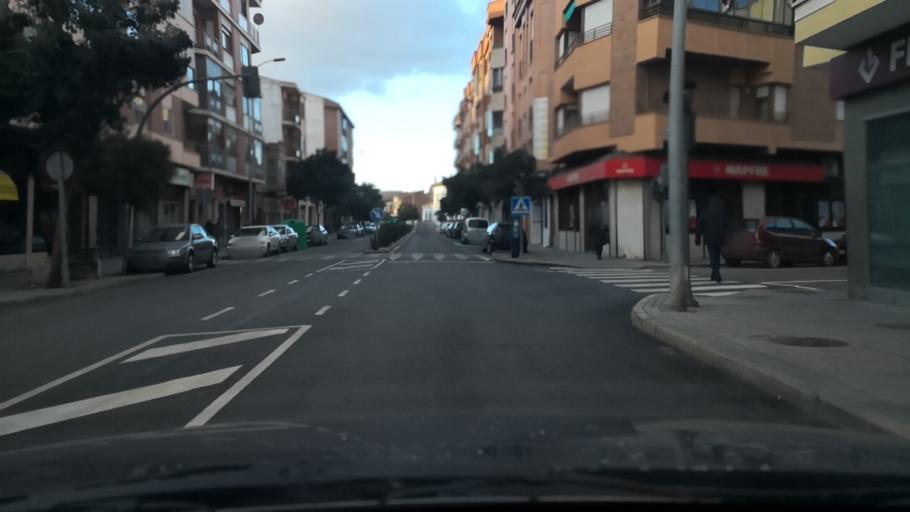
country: ES
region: Castille and Leon
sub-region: Provincia de Valladolid
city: Medina del Campo
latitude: 41.3080
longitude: -4.9119
